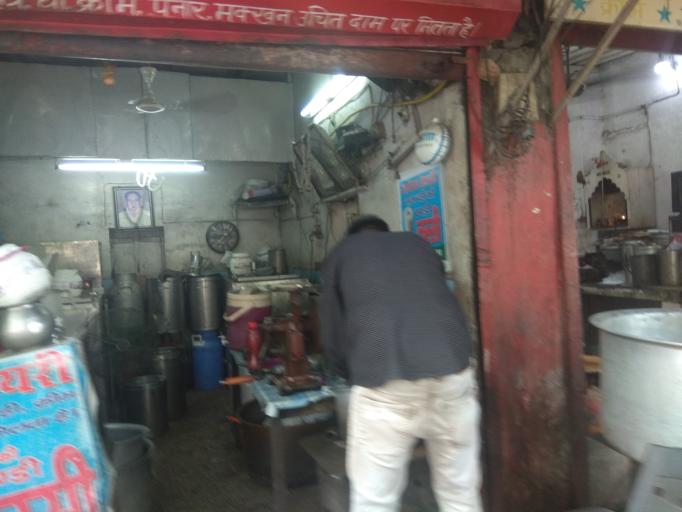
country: IN
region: NCT
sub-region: New Delhi
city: New Delhi
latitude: 28.5734
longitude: 77.2574
